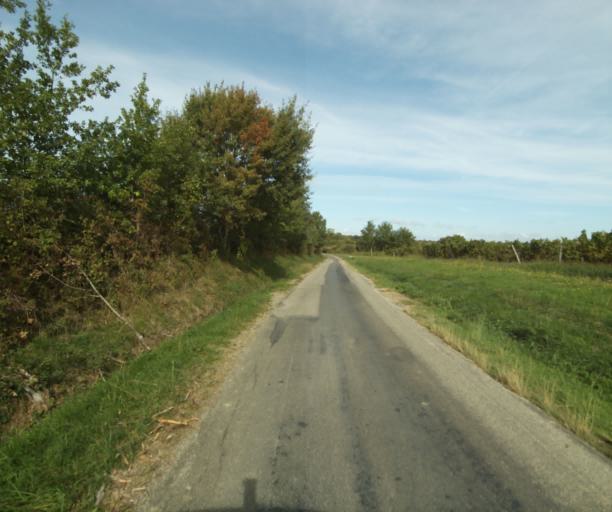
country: FR
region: Midi-Pyrenees
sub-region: Departement du Gers
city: Eauze
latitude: 43.8614
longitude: 0.1325
